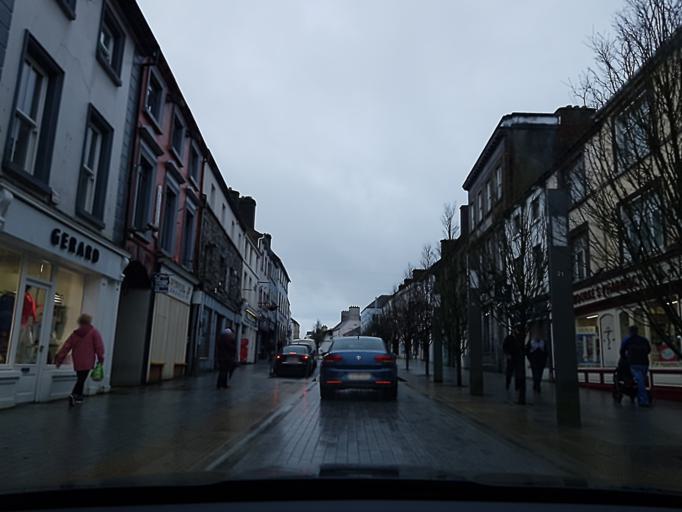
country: IE
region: Connaught
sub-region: Maigh Eo
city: Castlebar
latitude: 53.8566
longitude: -9.2985
